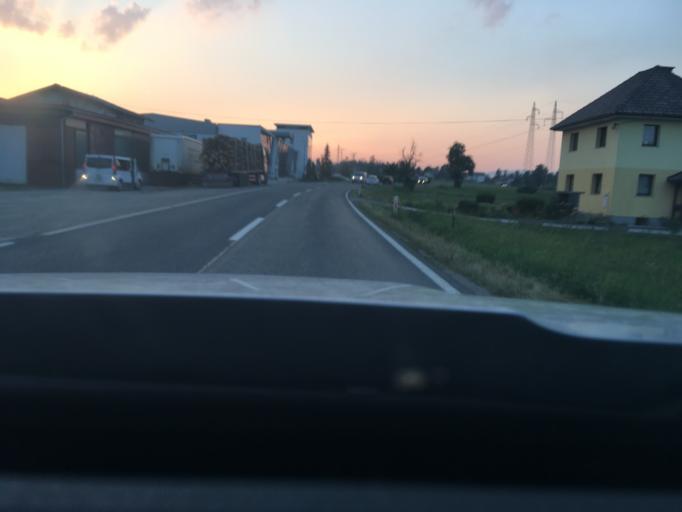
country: SI
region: Ribnica
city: Ribnica
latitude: 45.7144
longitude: 14.7477
